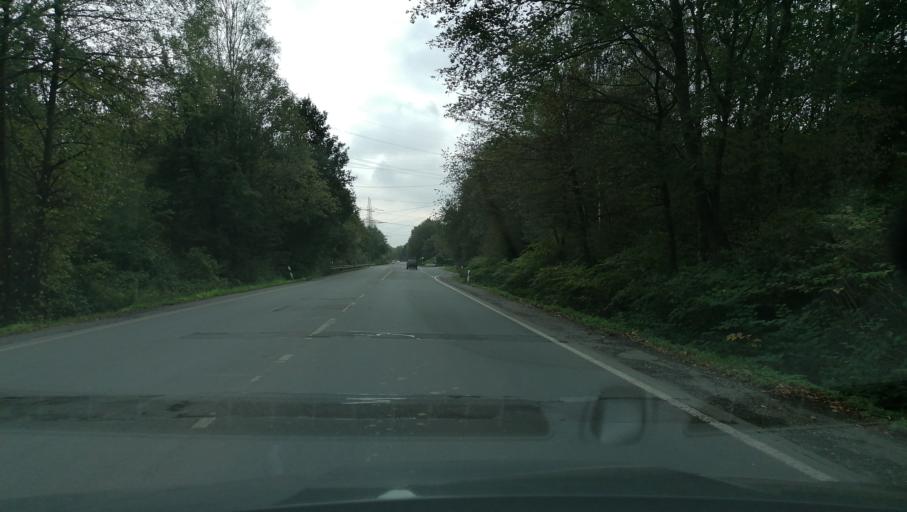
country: DE
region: North Rhine-Westphalia
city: Herten
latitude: 51.5582
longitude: 7.1366
